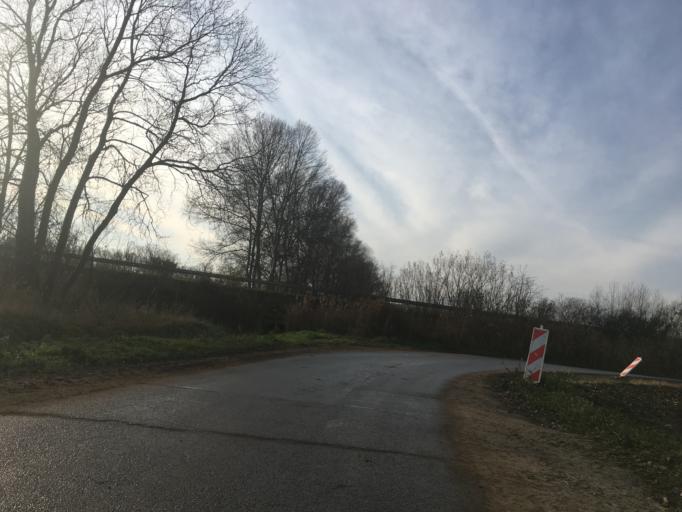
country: DE
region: Brandenburg
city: Bad Freienwalde
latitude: 52.7752
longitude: 14.0876
